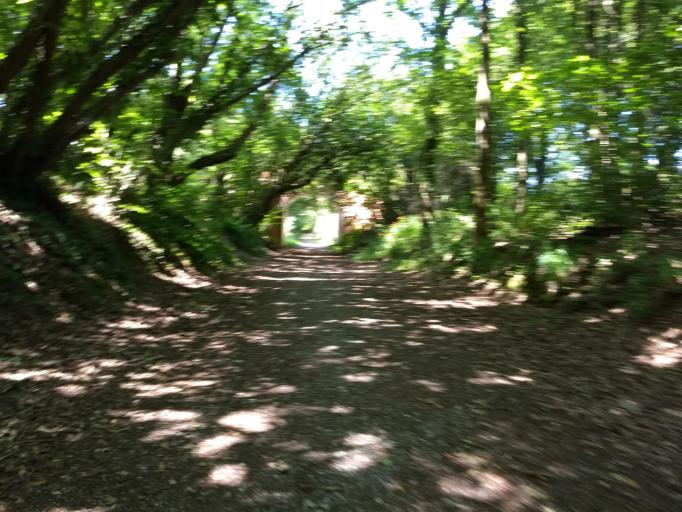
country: GB
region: England
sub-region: Isle of Wight
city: Newport
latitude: 50.7204
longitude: -1.2471
